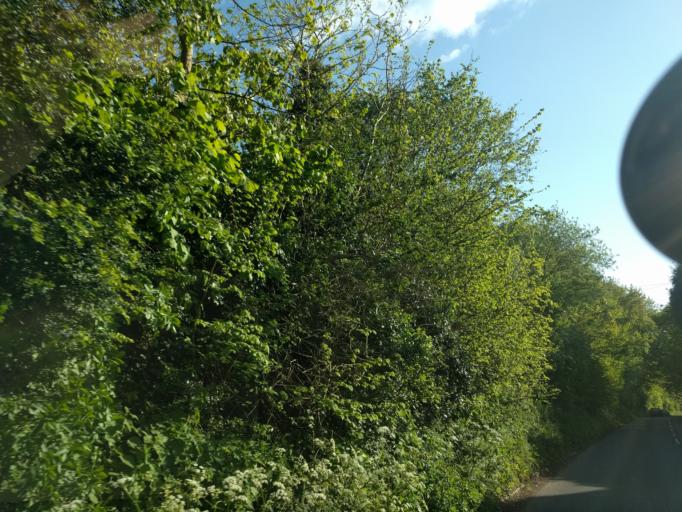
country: GB
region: England
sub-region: Wiltshire
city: Devizes
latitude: 51.3273
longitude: -2.0049
